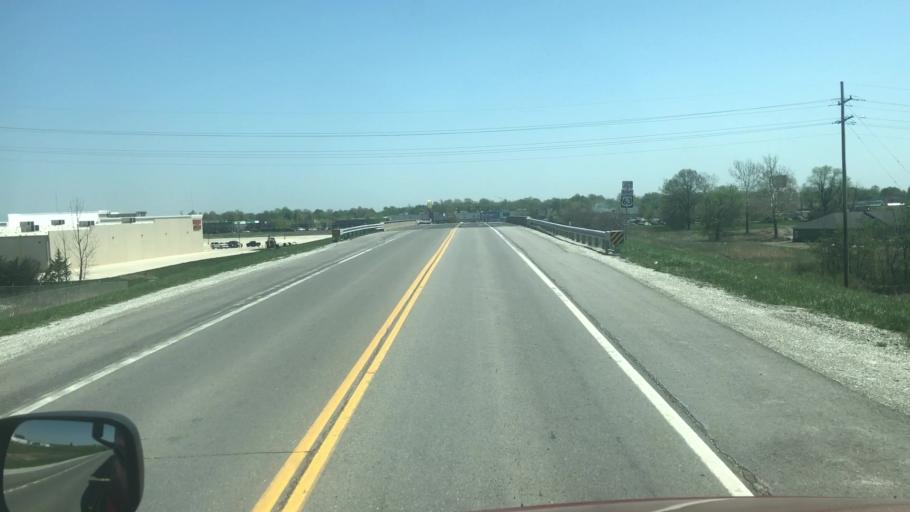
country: US
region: Missouri
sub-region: Adair County
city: Kirksville
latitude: 40.2166
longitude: -92.5875
